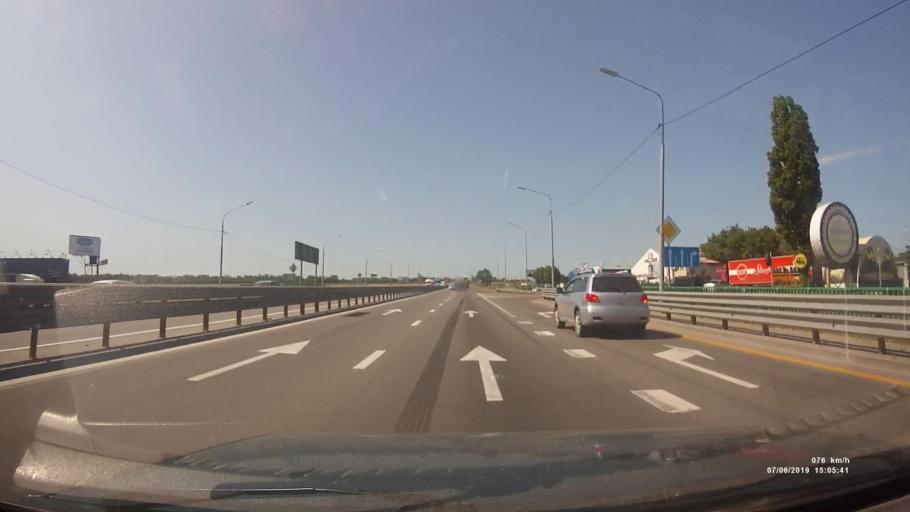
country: RU
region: Rostov
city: Aksay
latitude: 47.2752
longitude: 39.8503
